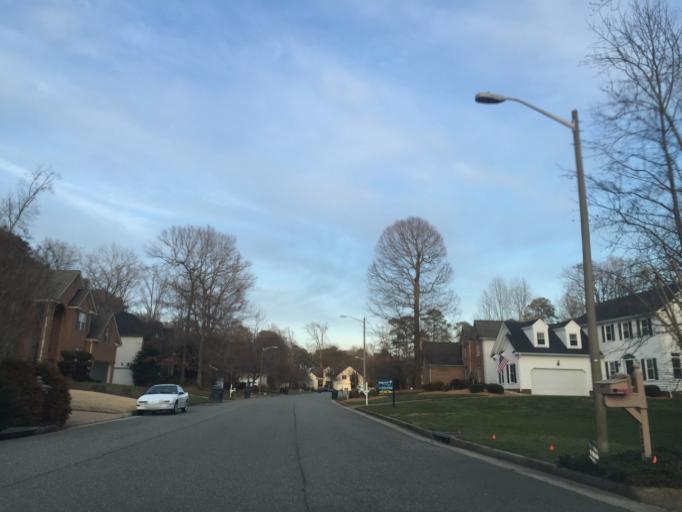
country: US
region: Virginia
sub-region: York County
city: Yorktown
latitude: 37.0994
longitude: -76.5053
